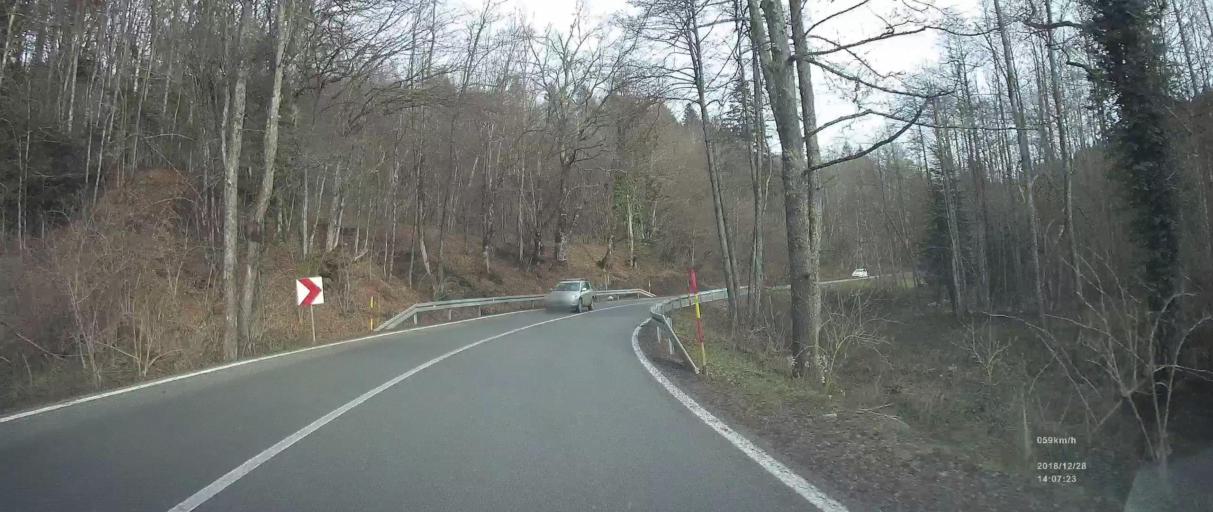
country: SI
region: Kostel
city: Kostel
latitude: 45.4445
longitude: 14.9478
